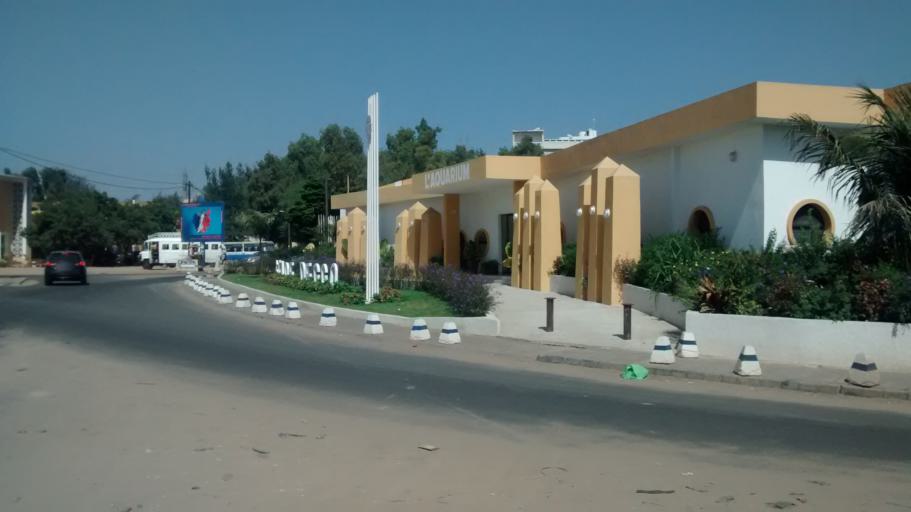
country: SN
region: Dakar
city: Grand Dakar
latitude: 14.7317
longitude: -17.4348
